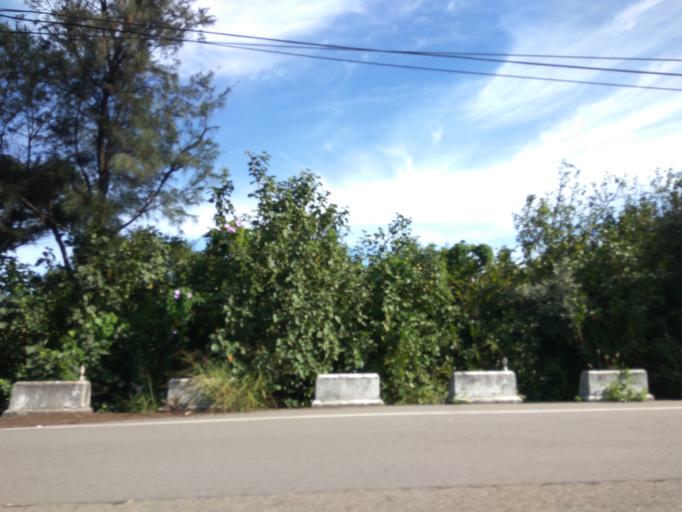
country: TW
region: Taiwan
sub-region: Hsinchu
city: Zhubei
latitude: 25.0327
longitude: 121.0539
